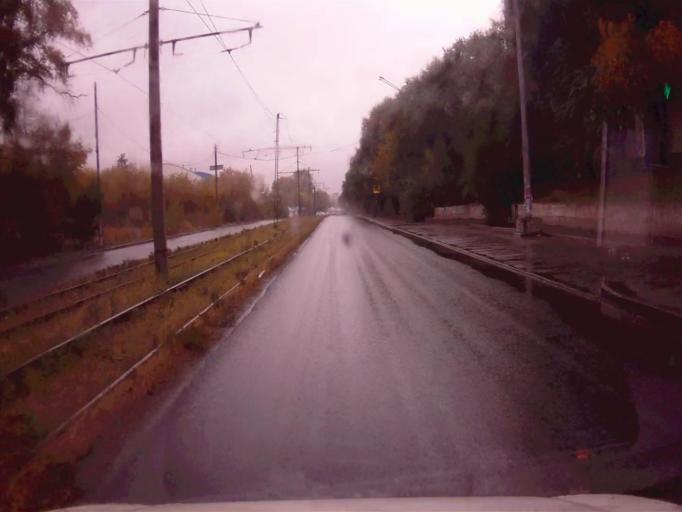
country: RU
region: Chelyabinsk
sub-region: Gorod Chelyabinsk
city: Chelyabinsk
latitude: 55.1756
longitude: 61.4151
